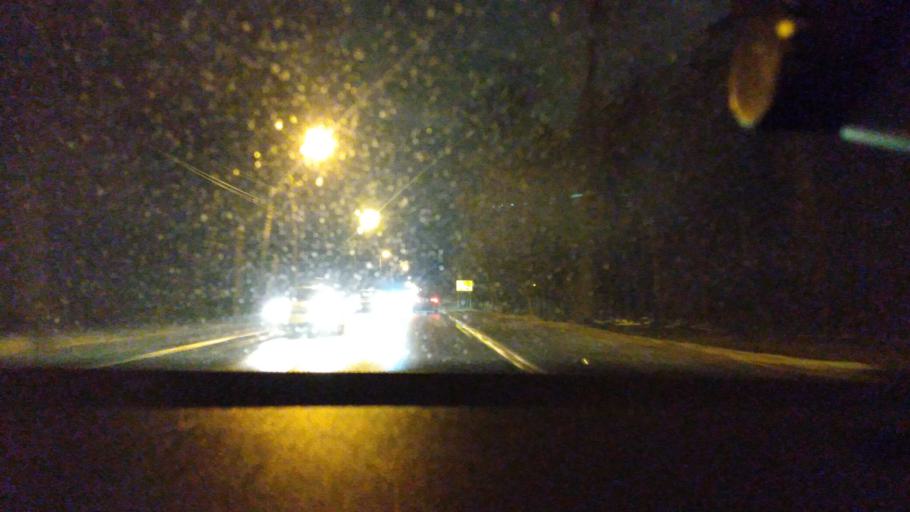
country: RU
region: Moskovskaya
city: Saltykovka
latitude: 55.7869
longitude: 37.9315
